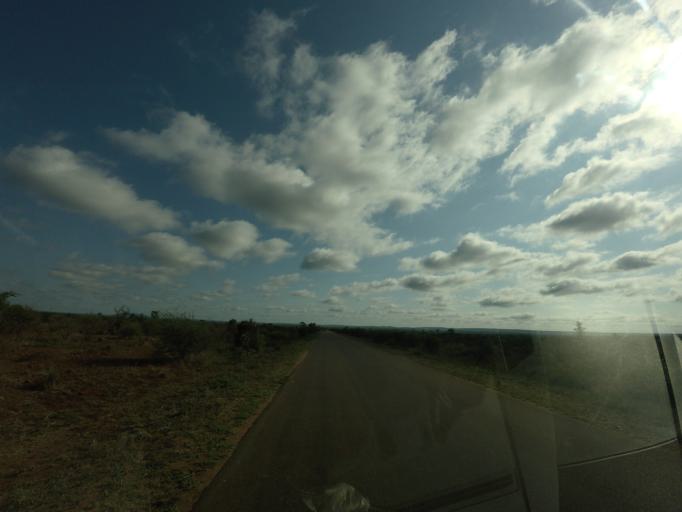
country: ZA
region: Mpumalanga
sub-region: Ehlanzeni District
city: Komatipoort
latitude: -25.1745
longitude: 31.9153
